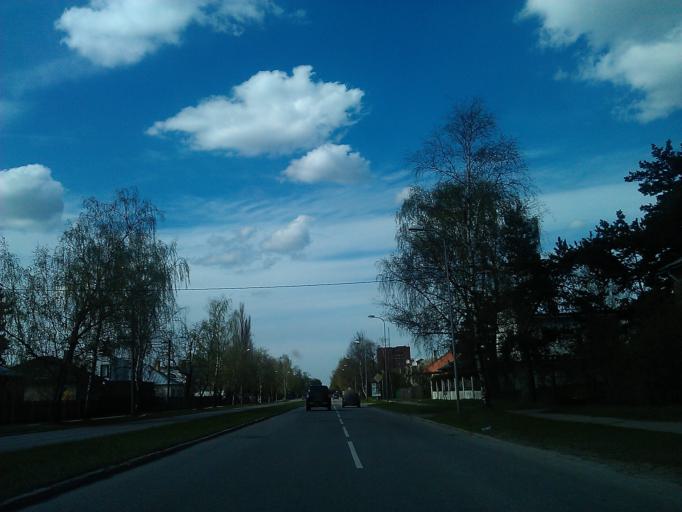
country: LV
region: Riga
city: Jaunciems
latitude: 56.9697
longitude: 24.1946
